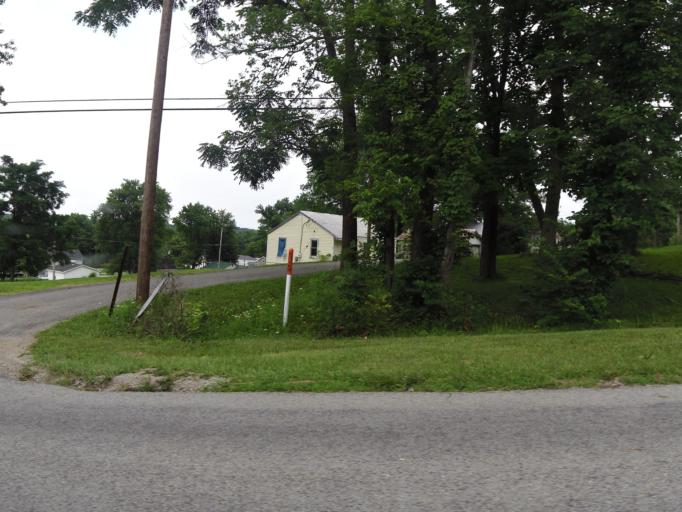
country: US
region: Ohio
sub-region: Warren County
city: Waynesville
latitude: 39.5246
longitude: -84.0770
